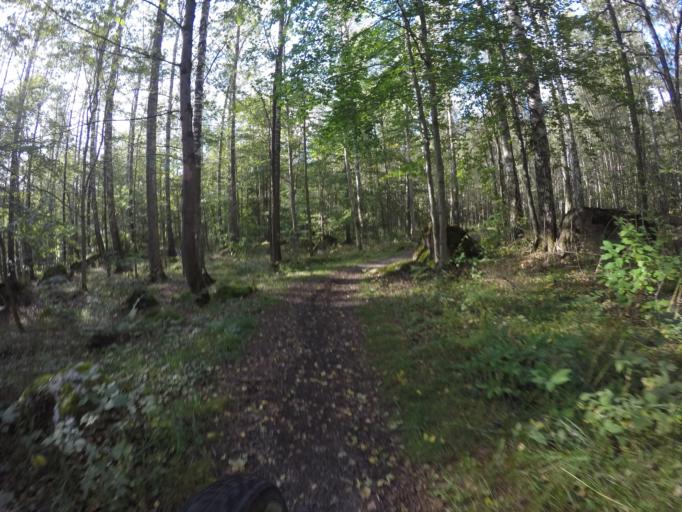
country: SE
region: Vaestmanland
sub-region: Kopings Kommun
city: Koping
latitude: 59.5082
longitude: 16.0147
